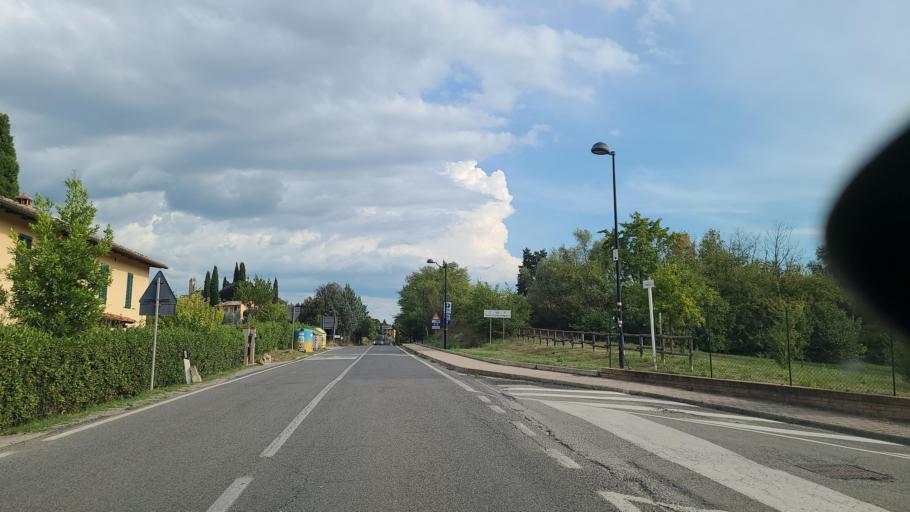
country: IT
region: Tuscany
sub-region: Provincia di Siena
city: San Gimignano
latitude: 43.4759
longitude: 11.0298
